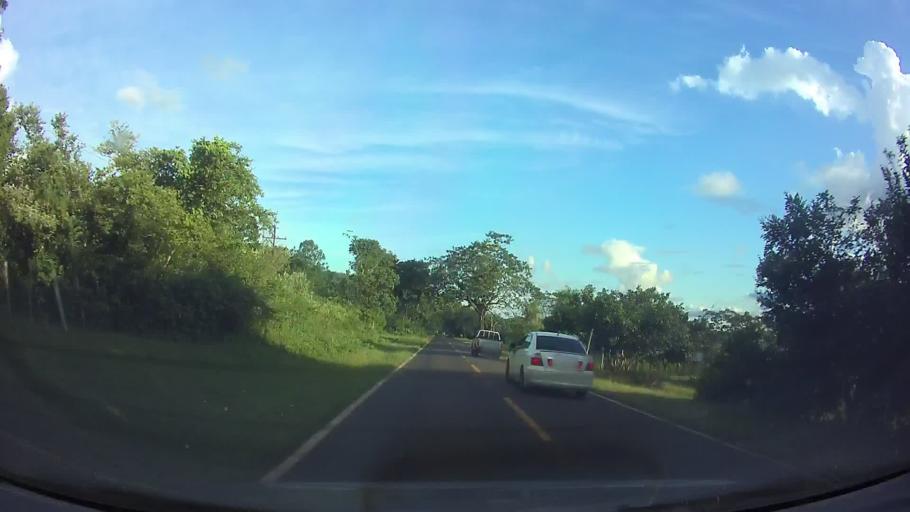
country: PY
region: Paraguari
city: Ybycui
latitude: -25.9644
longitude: -57.0847
